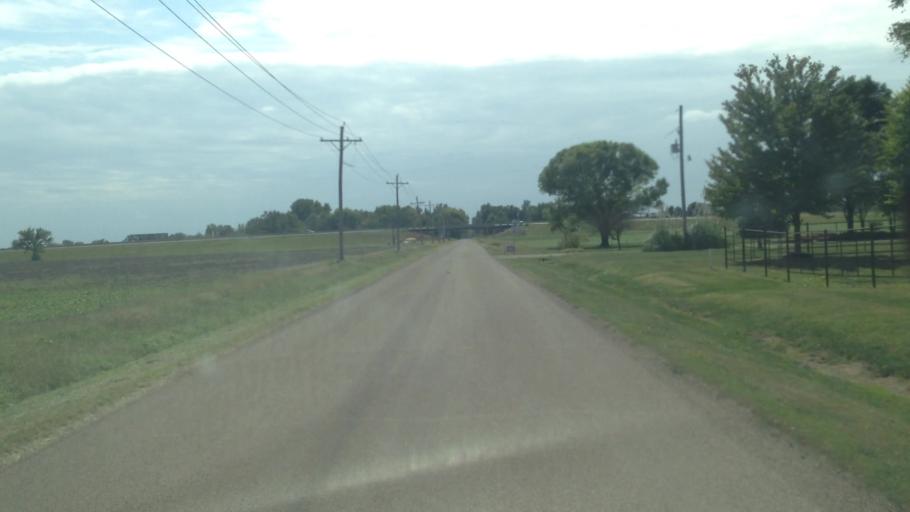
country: US
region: Kansas
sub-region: Douglas County
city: Lawrence
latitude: 38.9978
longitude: -95.2241
